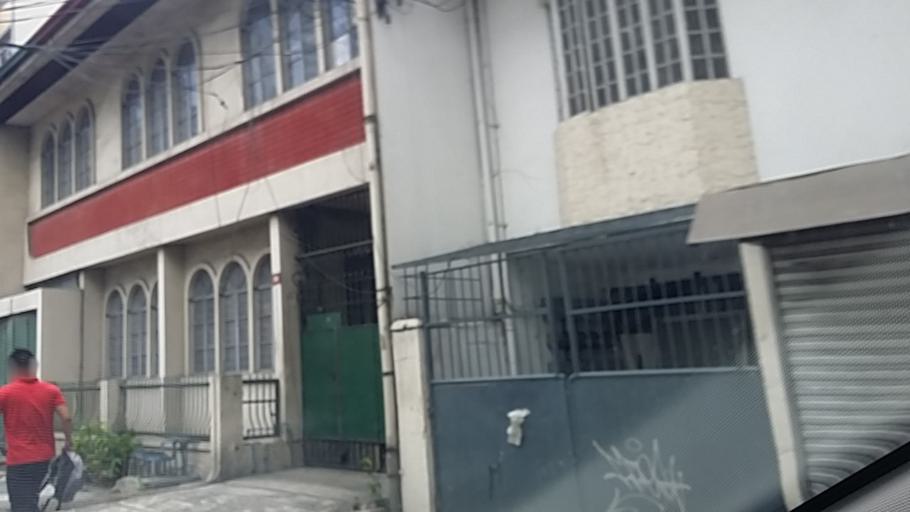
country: PH
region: Metro Manila
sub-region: Mandaluyong
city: Mandaluyong City
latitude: 14.5779
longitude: 121.0505
